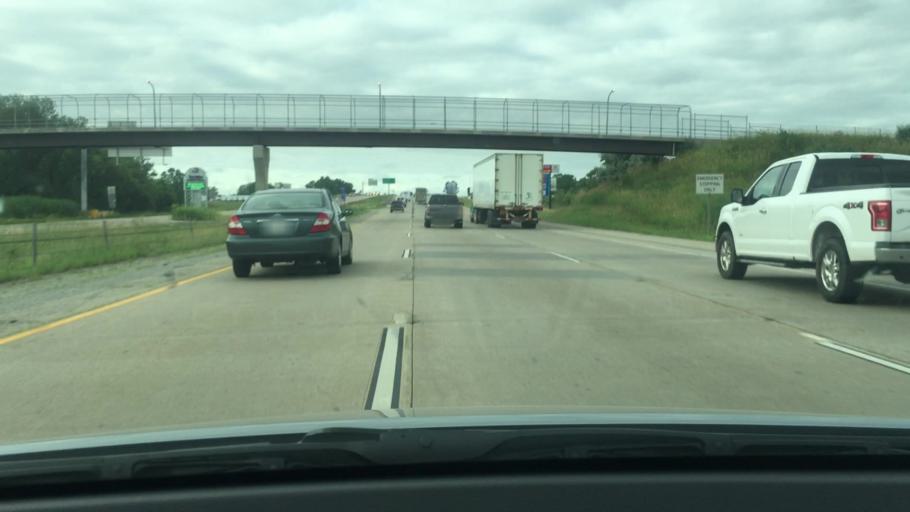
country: US
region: Wisconsin
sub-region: Outagamie County
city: Appleton
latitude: 44.2845
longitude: -88.4664
